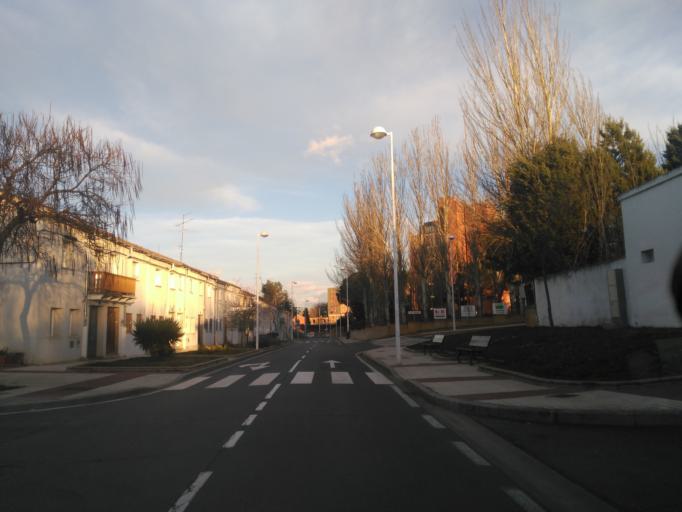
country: ES
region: Castille and Leon
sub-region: Provincia de Salamanca
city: Salamanca
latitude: 40.9496
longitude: -5.6657
